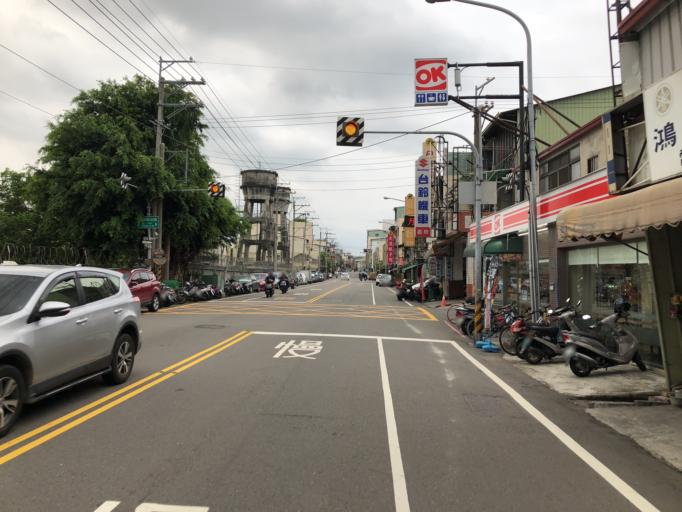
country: TW
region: Taiwan
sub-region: Taichung City
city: Taichung
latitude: 24.1180
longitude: 120.7331
